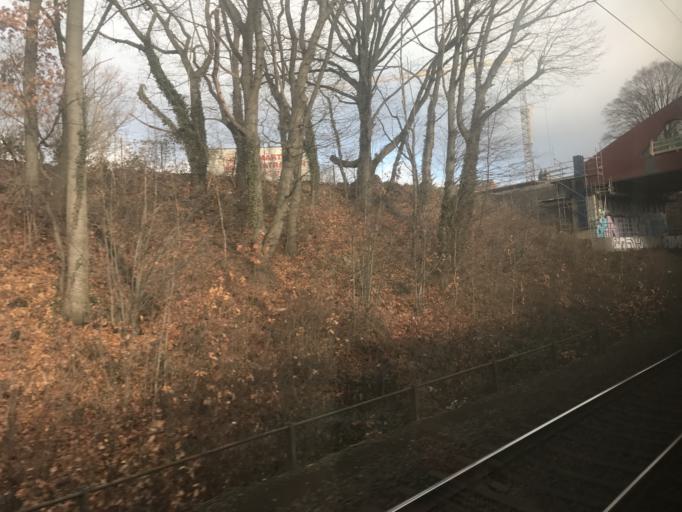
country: DE
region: North Rhine-Westphalia
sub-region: Regierungsbezirk Arnsberg
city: Bochum
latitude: 51.4847
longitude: 7.2488
